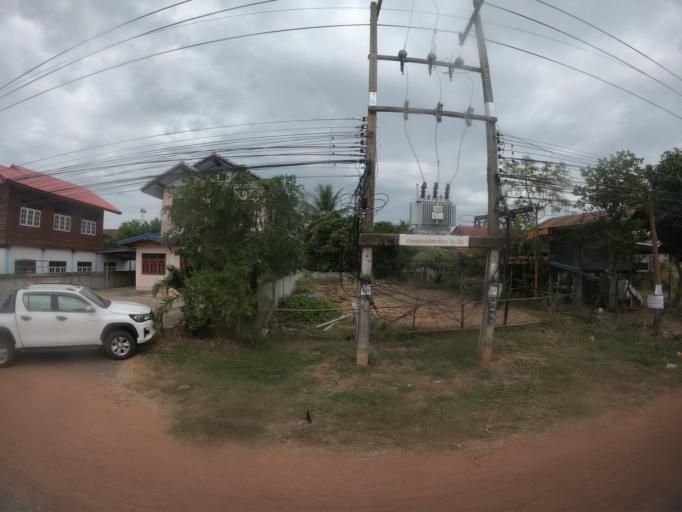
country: TH
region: Maha Sarakham
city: Kantharawichai
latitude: 16.3376
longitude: 103.1904
